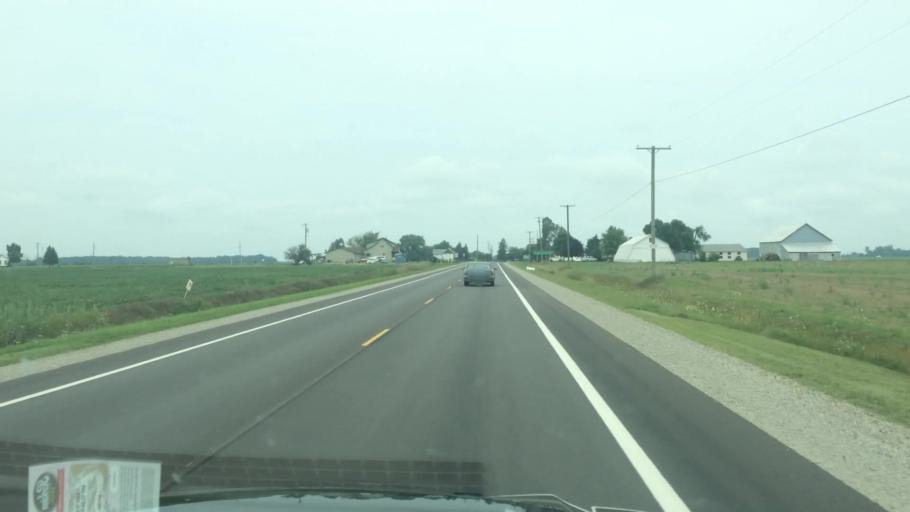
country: US
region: Michigan
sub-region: Huron County
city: Bad Axe
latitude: 44.0005
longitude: -83.0078
